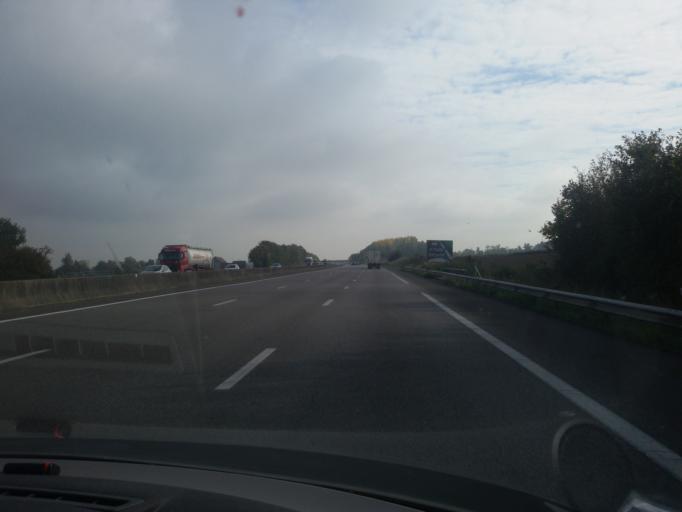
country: FR
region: Haute-Normandie
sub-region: Departement de l'Eure
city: Ande
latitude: 49.1647
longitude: 1.2580
